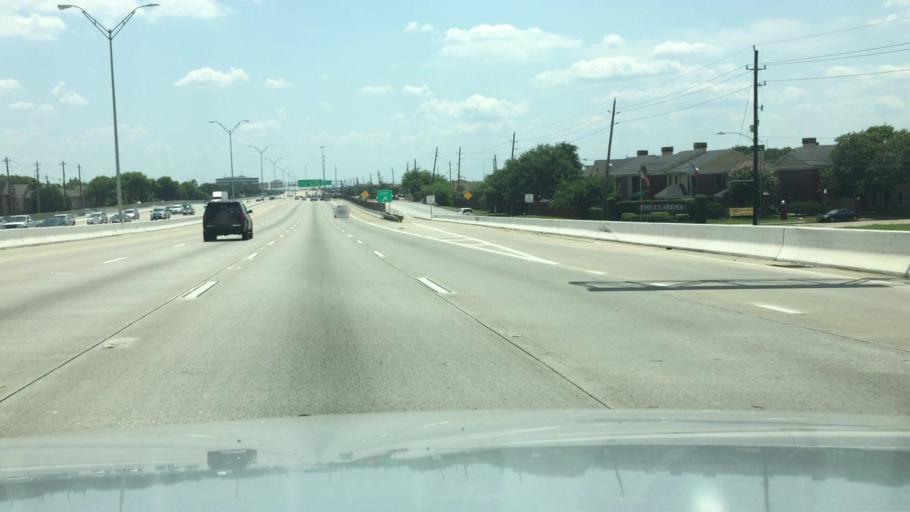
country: US
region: Texas
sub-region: Fort Bend County
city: Meadows Place
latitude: 29.6872
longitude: -95.5580
